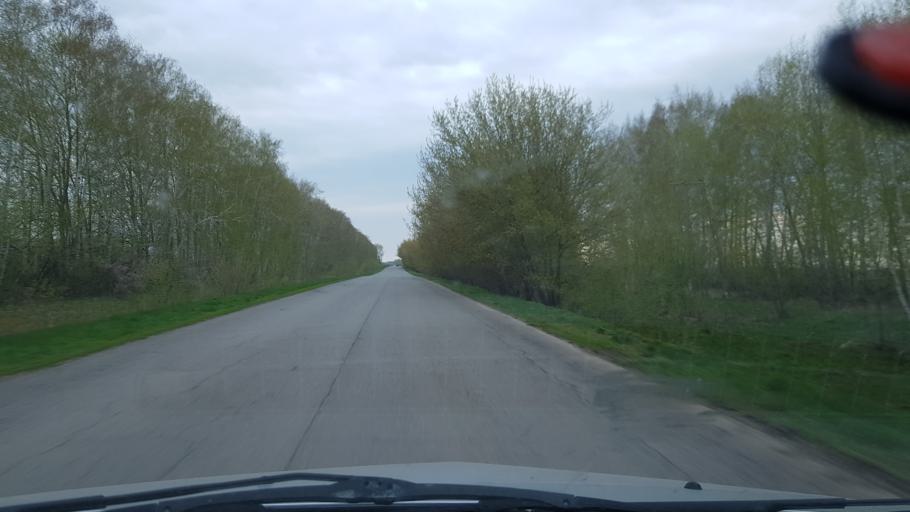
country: RU
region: Samara
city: Podstepki
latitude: 53.6647
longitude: 49.1778
